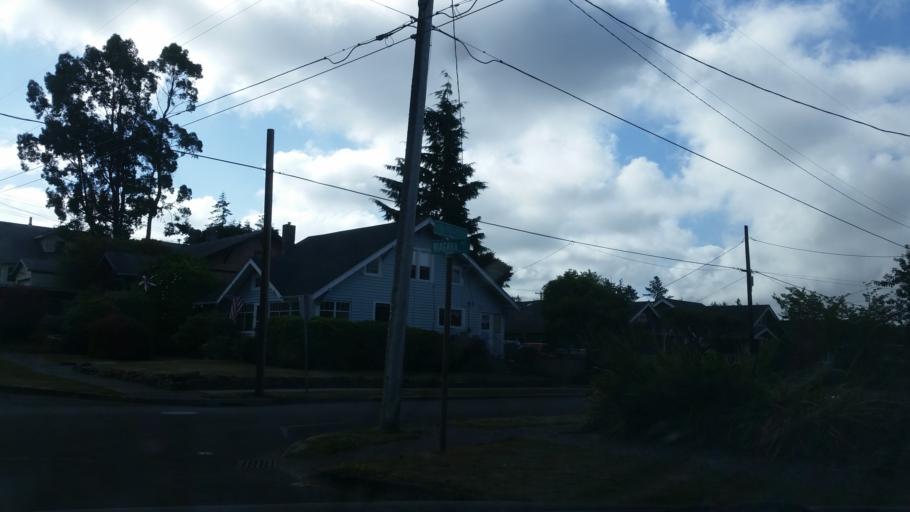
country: US
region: Oregon
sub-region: Clatsop County
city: Astoria
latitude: 46.1813
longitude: -123.8372
